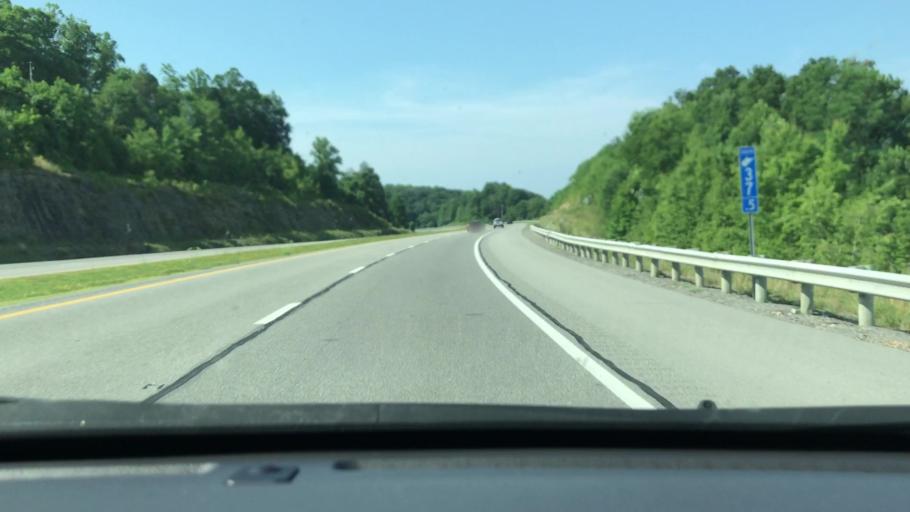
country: US
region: West Virginia
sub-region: Nicholas County
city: Summersville
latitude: 38.2259
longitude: -80.8491
